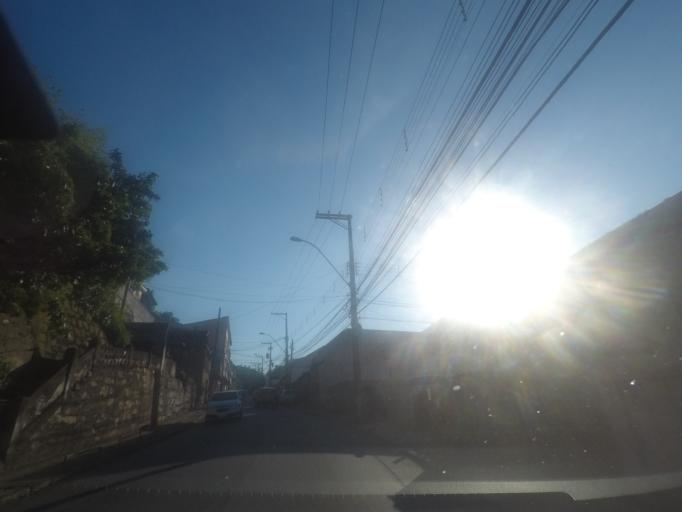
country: BR
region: Rio de Janeiro
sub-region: Petropolis
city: Petropolis
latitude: -22.4916
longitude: -43.1569
